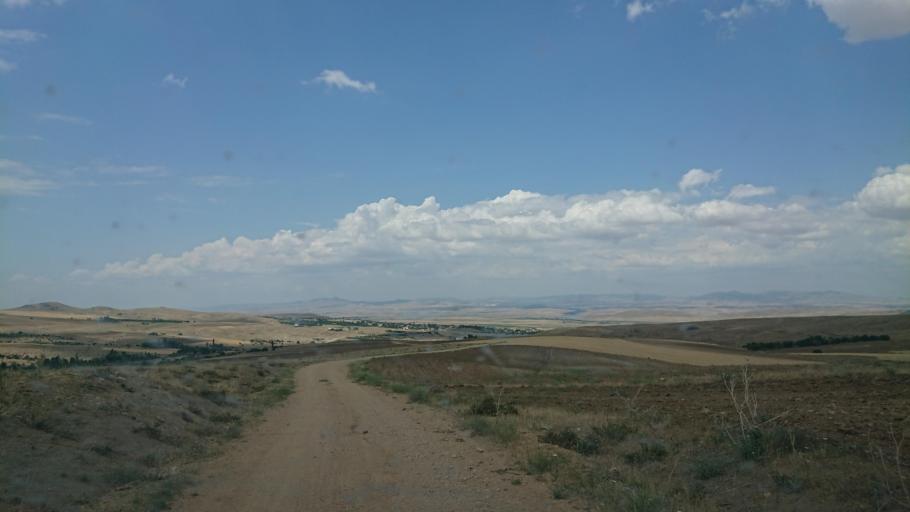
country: TR
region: Aksaray
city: Agacoren
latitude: 38.9315
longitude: 33.8877
